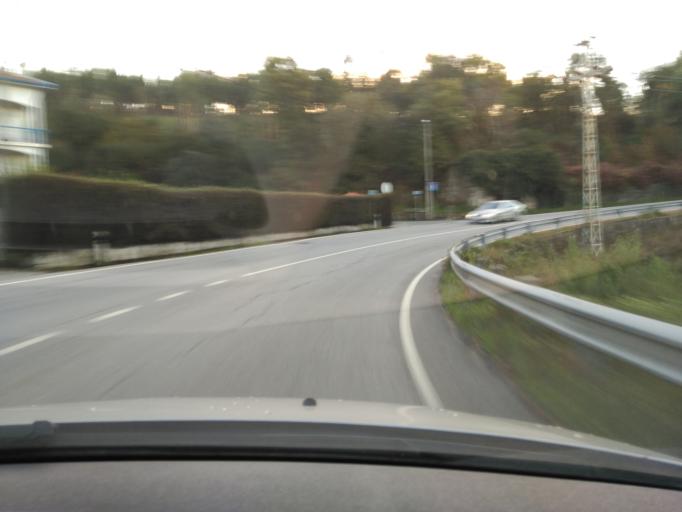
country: PT
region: Braga
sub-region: Braga
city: Braga
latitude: 41.5004
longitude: -8.4150
